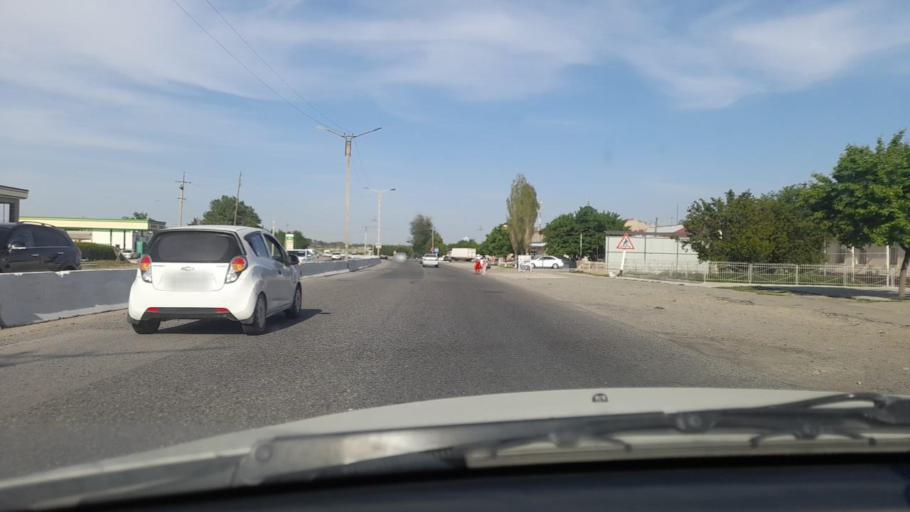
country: UZ
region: Samarqand
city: Bulung'ur
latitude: 39.7709
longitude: 67.2739
